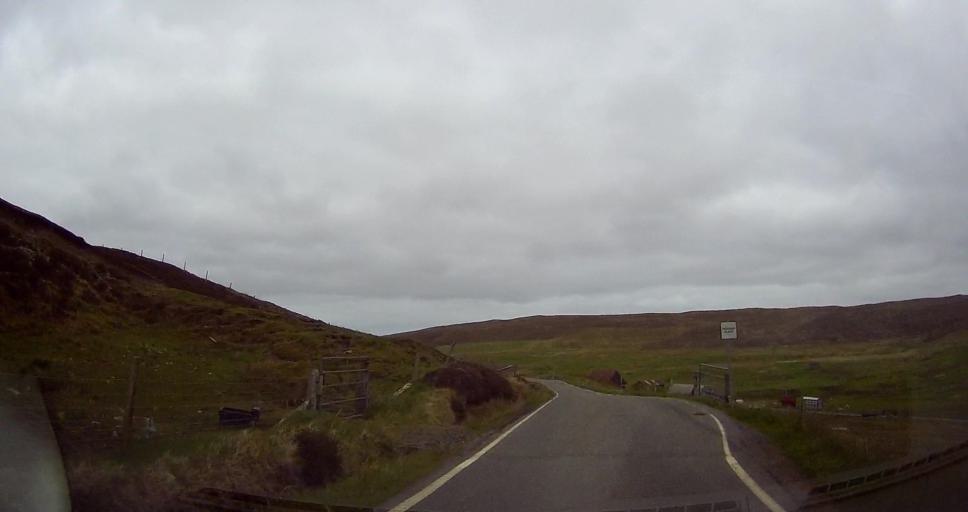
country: GB
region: Scotland
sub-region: Shetland Islands
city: Lerwick
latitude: 60.3430
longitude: -1.2804
